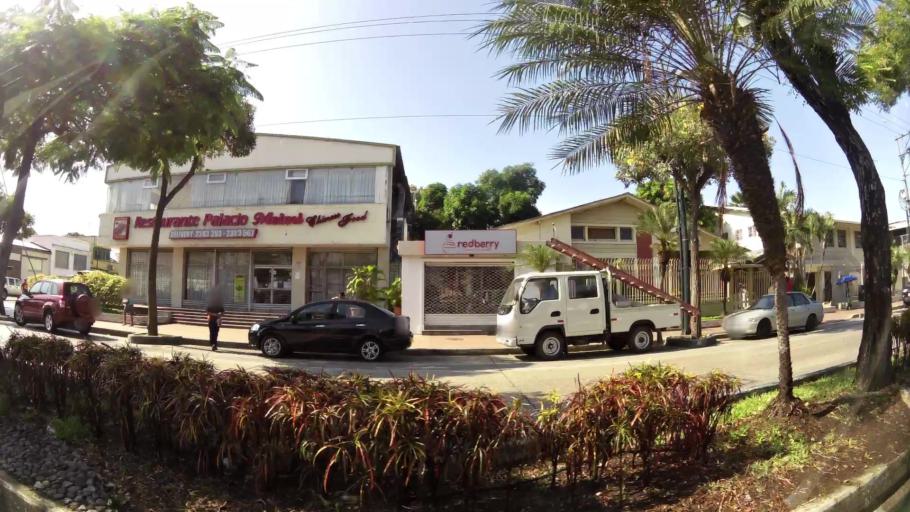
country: EC
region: Guayas
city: Guayaquil
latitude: -2.1693
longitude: -79.9093
